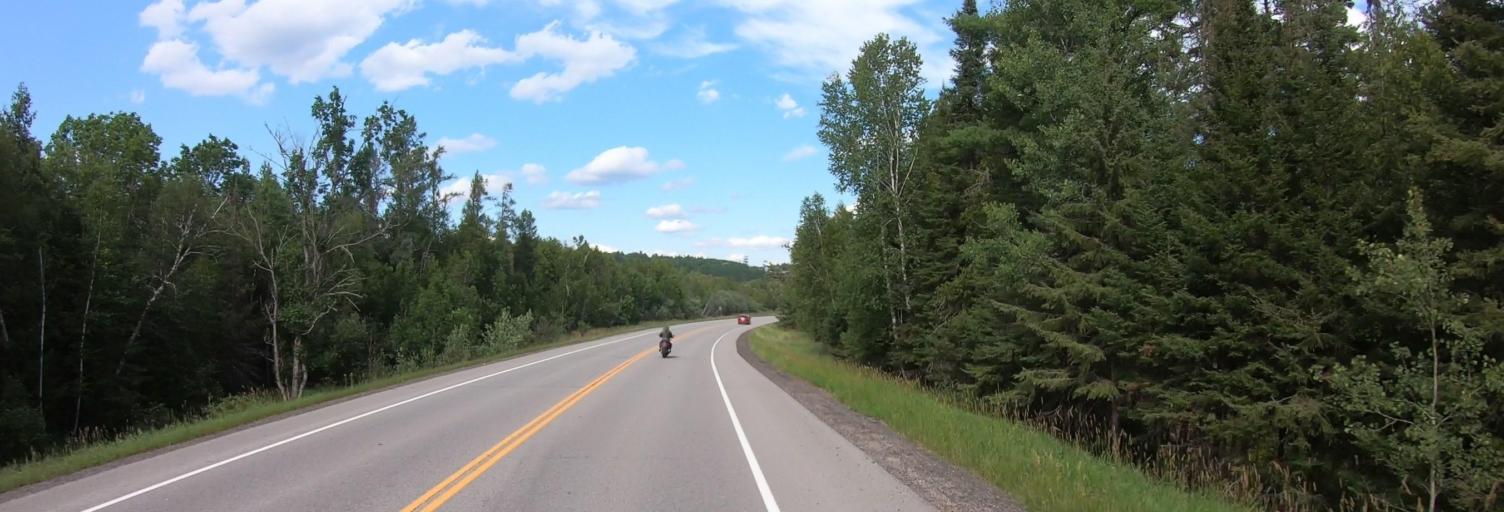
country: US
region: Minnesota
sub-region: Saint Louis County
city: Aurora
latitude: 47.8098
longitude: -92.2552
